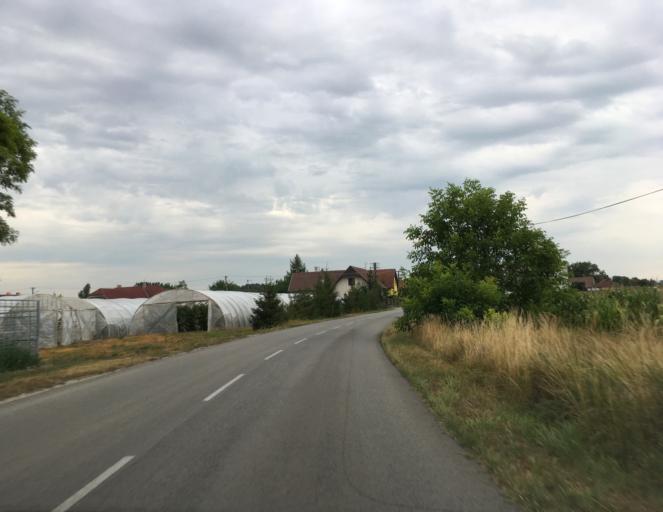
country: SK
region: Trnavsky
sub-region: Okres Dunajska Streda
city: Velky Meder
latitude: 47.9228
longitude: 17.6979
